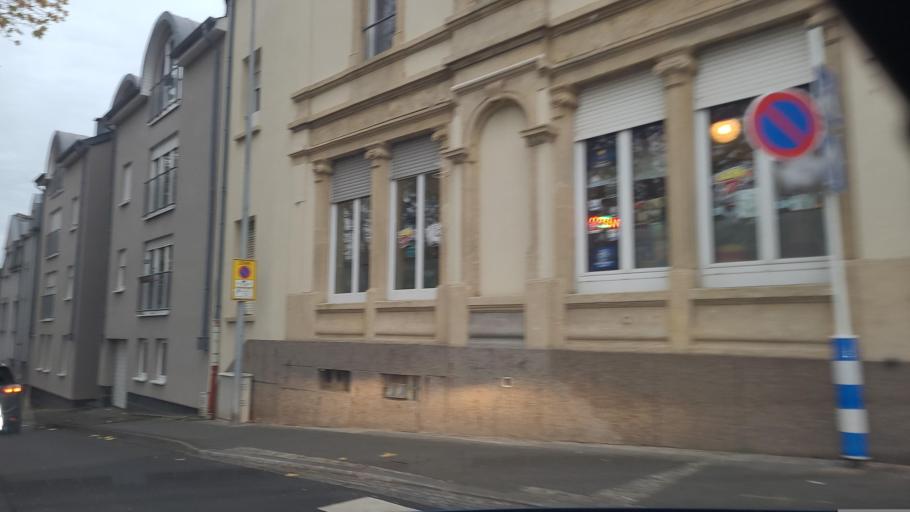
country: LU
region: Luxembourg
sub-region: Canton d'Esch-sur-Alzette
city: Obercorn
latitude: 49.5150
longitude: 5.8967
